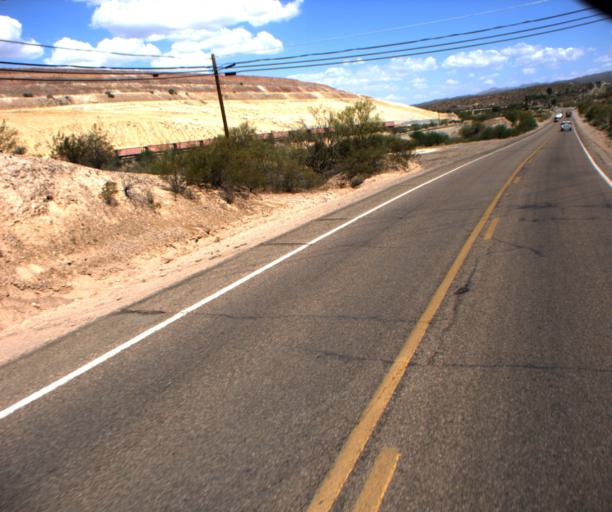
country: US
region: Arizona
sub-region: Pinal County
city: Kearny
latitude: 32.9936
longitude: -110.7831
